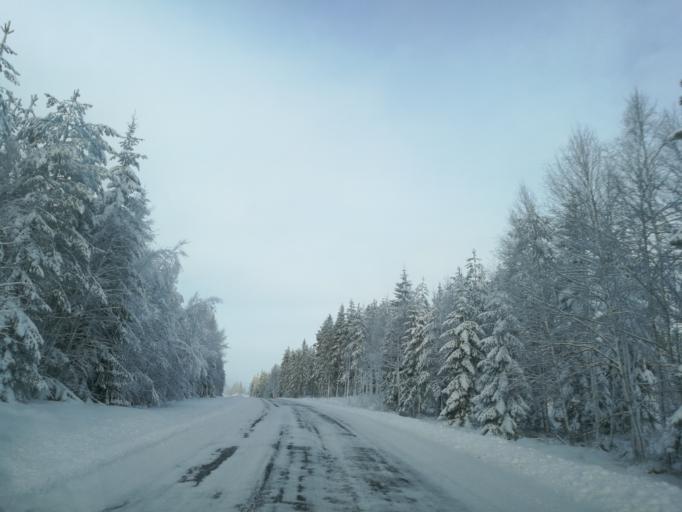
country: SE
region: Vaermland
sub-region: Torsby Kommun
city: Torsby
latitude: 60.6173
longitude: 12.7160
